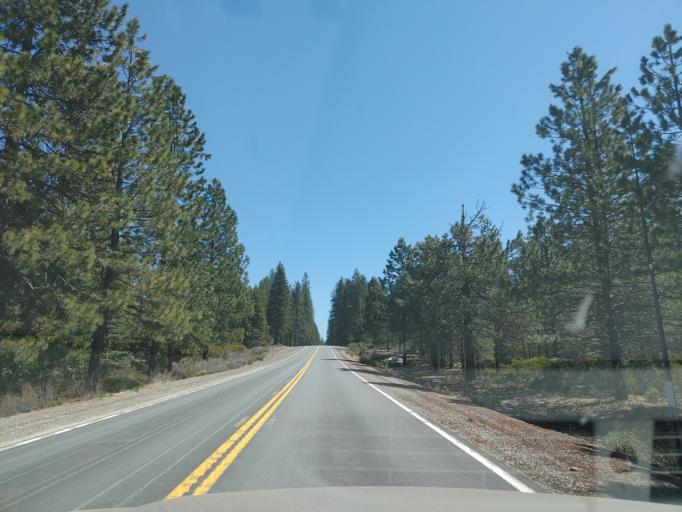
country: US
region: California
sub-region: Siskiyou County
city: McCloud
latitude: 41.2661
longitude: -121.9256
